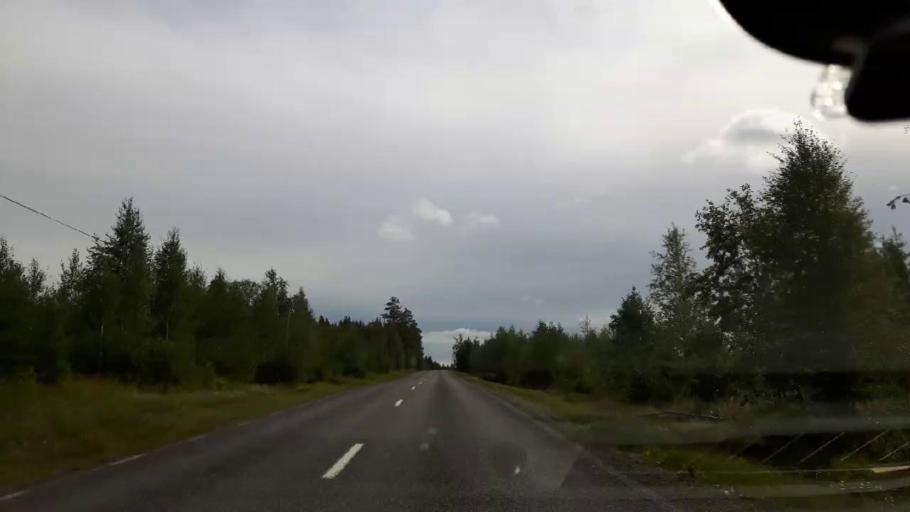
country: SE
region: Jaemtland
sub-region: Ragunda Kommun
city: Hammarstrand
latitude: 63.1358
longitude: 15.8729
